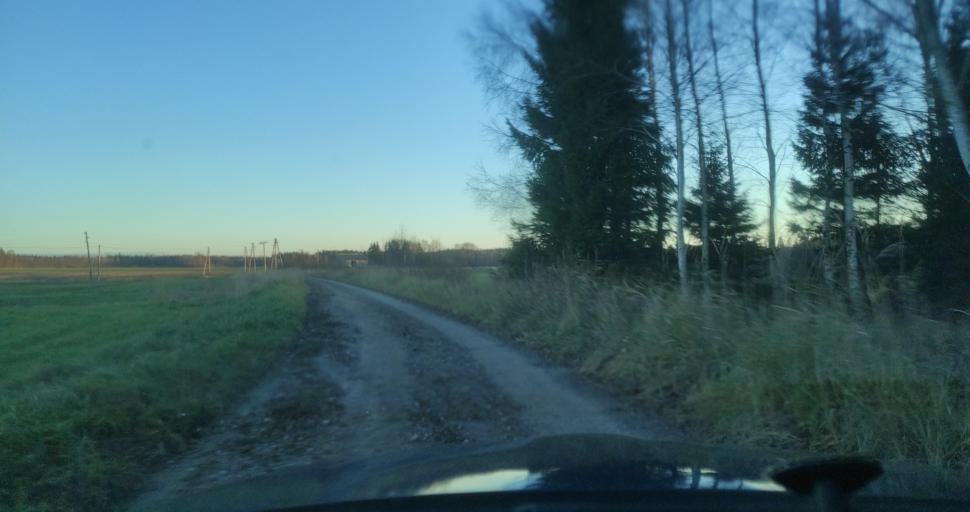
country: LV
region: Dundaga
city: Dundaga
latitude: 57.3883
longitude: 22.0870
